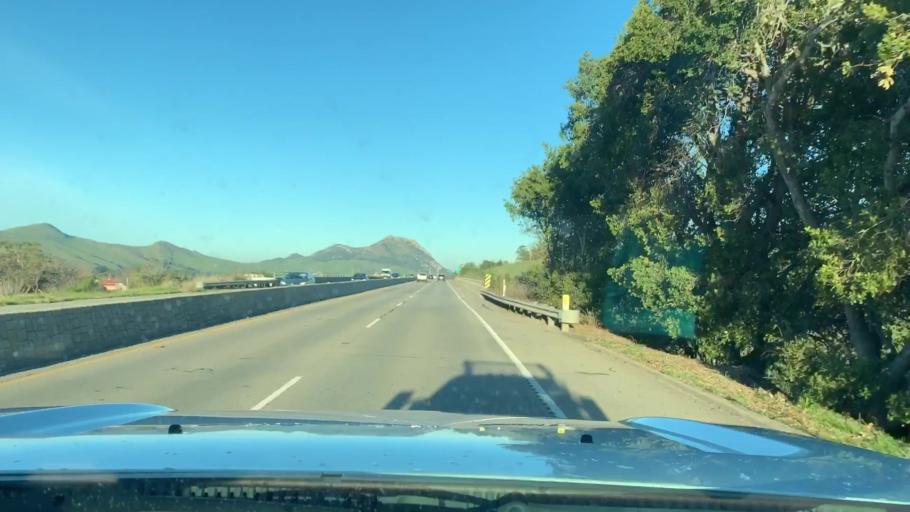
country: US
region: California
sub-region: San Luis Obispo County
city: San Luis Obispo
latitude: 35.3224
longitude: -120.7192
